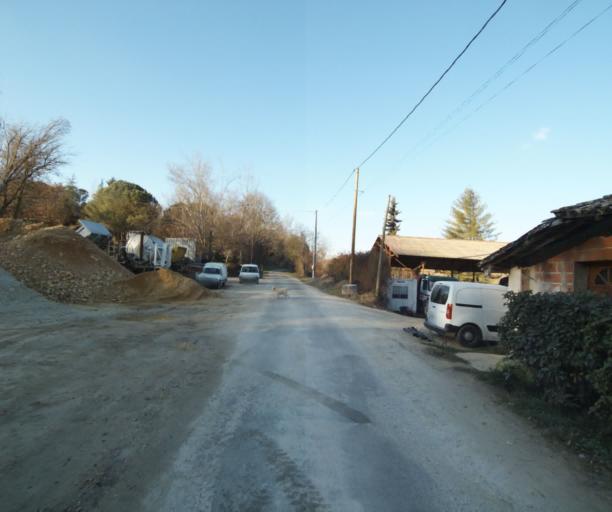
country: FR
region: Midi-Pyrenees
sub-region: Departement du Tarn-et-Garonne
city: Moissac
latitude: 44.1308
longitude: 1.0889
